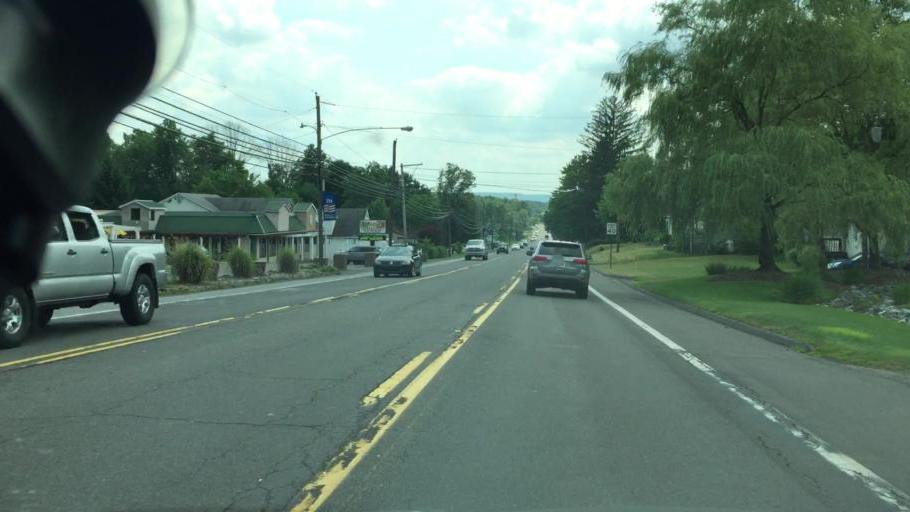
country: US
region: Pennsylvania
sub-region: Luzerne County
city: Mountain Top
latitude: 41.1533
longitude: -75.8933
